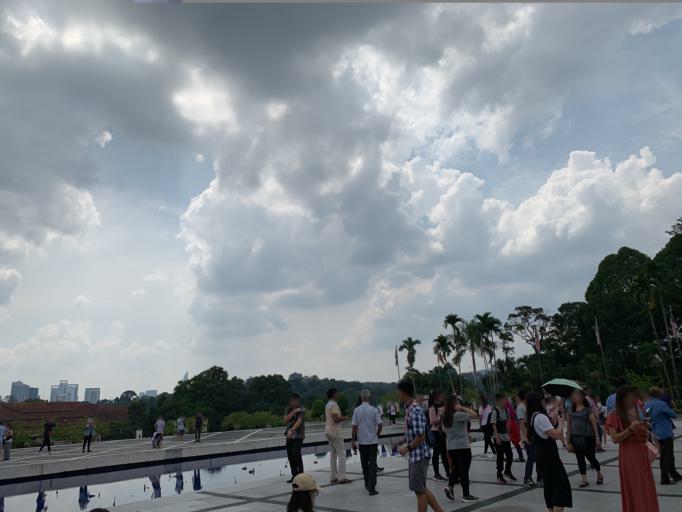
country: MY
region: Kuala Lumpur
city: Kuala Lumpur
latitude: 3.1488
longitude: 101.6840
